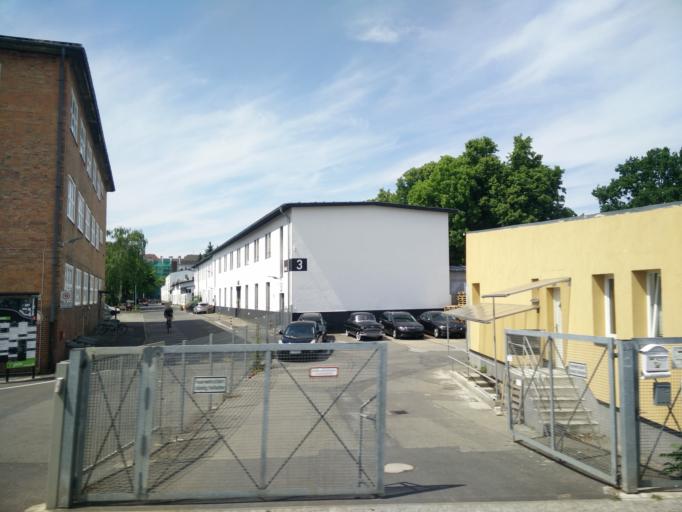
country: DE
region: Berlin
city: Berlin Schoeneberg
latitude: 52.4826
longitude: 13.3675
